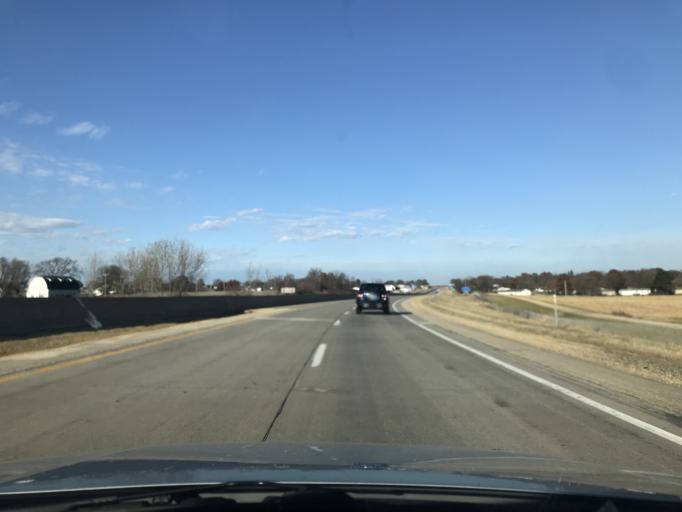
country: US
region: Iowa
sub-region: Jackson County
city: Maquoketa
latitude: 42.0506
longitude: -90.6827
